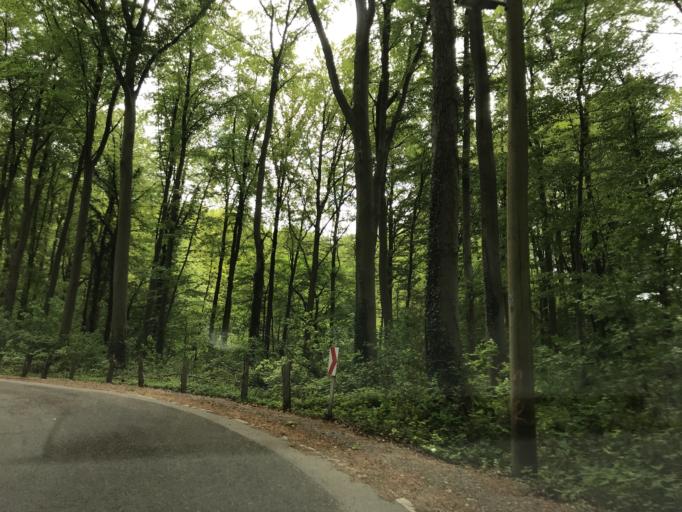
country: DE
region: North Rhine-Westphalia
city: Witten
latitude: 51.4796
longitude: 7.3690
